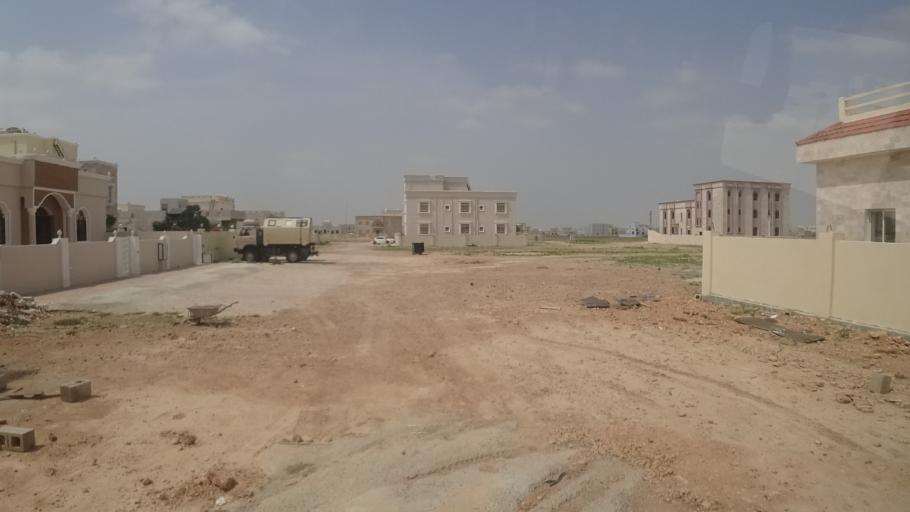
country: OM
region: Zufar
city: Salalah
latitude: 17.1012
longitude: 54.2137
